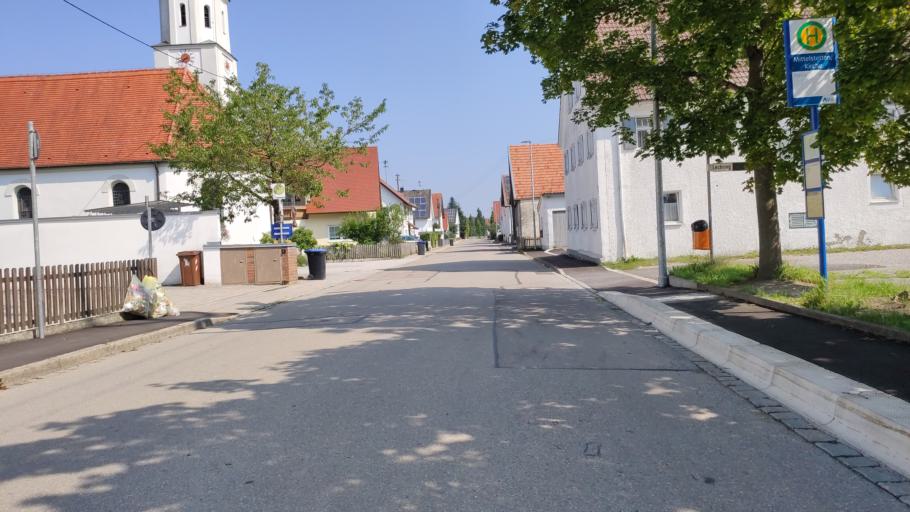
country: DE
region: Bavaria
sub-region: Swabia
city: Schwabmunchen
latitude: 48.2038
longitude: 10.7643
